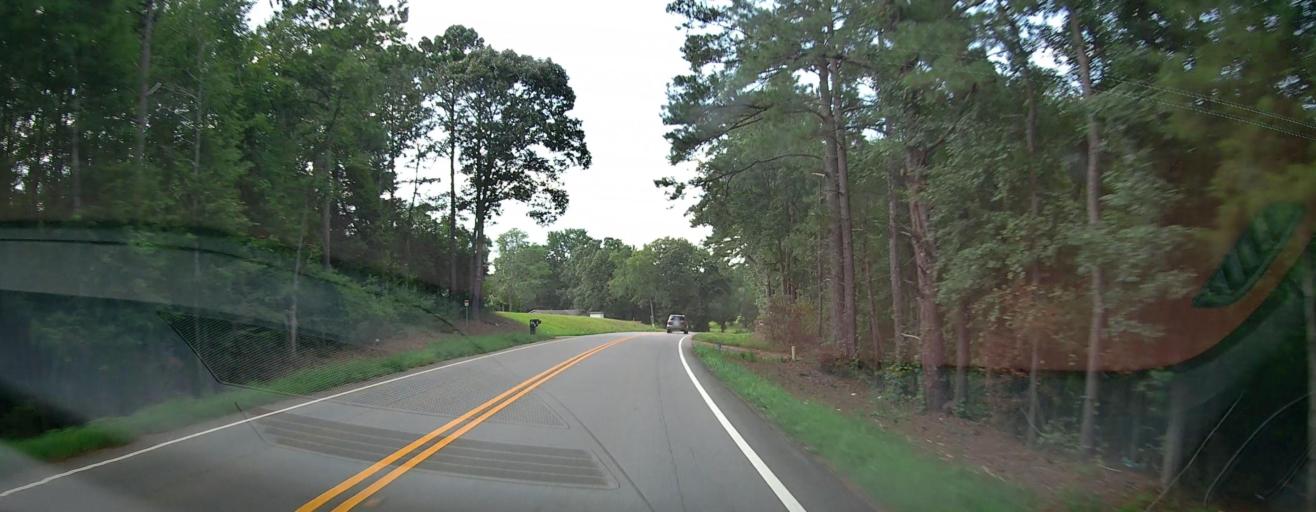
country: US
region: Georgia
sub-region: Monroe County
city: Forsyth
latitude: 33.0086
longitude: -83.9413
